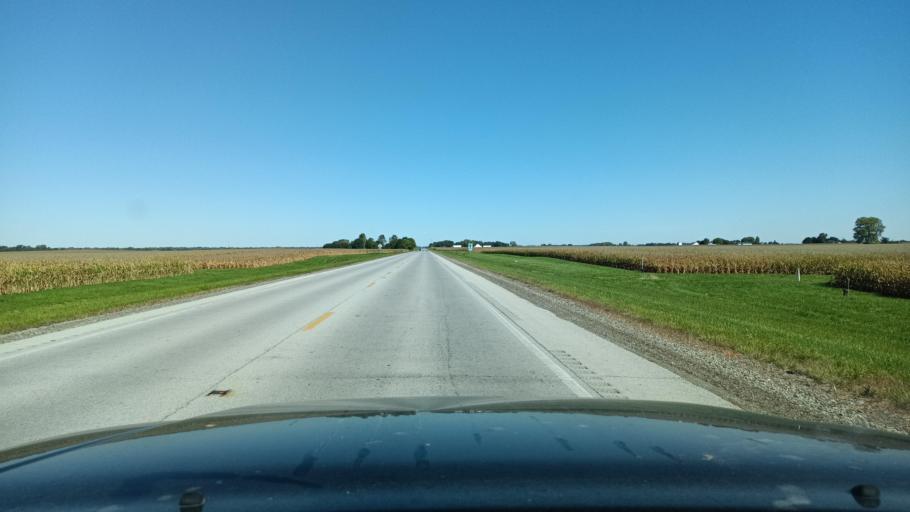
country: US
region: Illinois
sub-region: Champaign County
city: Philo
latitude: 40.0551
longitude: -88.1618
